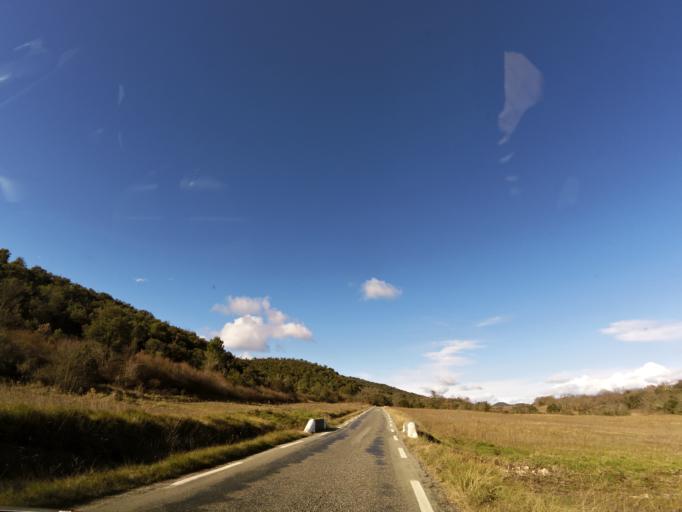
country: FR
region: Languedoc-Roussillon
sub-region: Departement du Gard
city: Sauve
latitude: 43.9755
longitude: 3.9488
